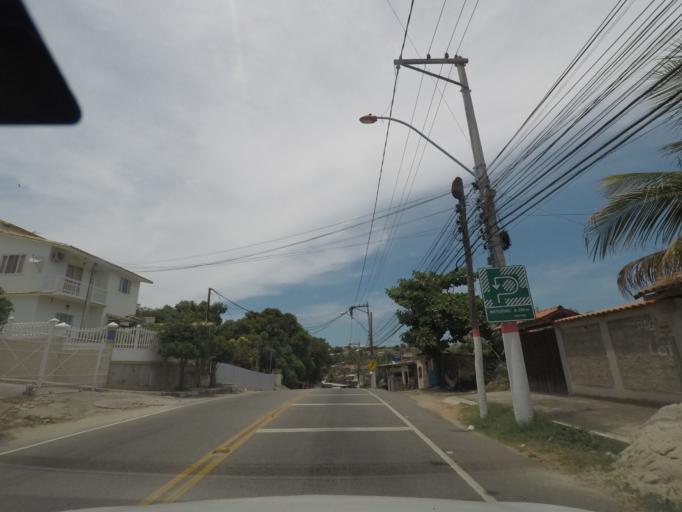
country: BR
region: Rio de Janeiro
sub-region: Marica
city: Marica
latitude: -22.9320
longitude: -42.8231
